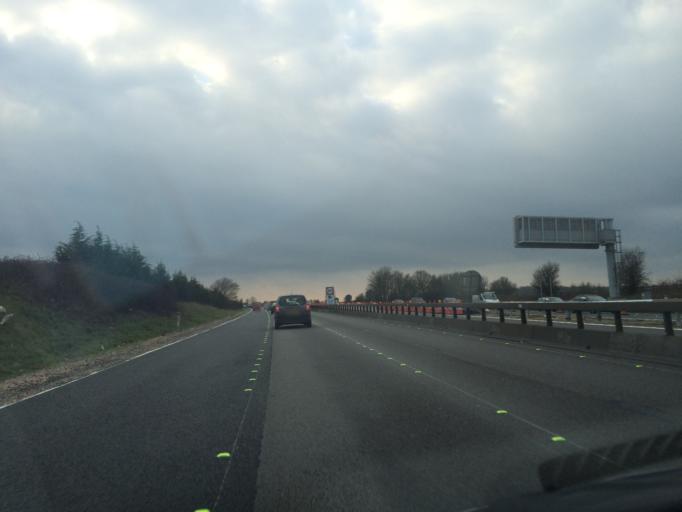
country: GB
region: England
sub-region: West Berkshire
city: Winterbourne
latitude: 51.4557
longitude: -1.3455
